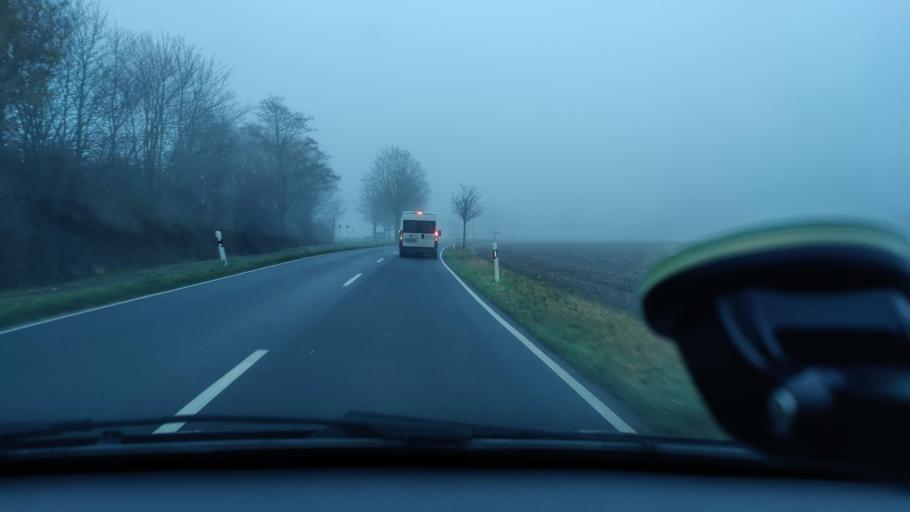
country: DE
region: North Rhine-Westphalia
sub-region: Regierungsbezirk Dusseldorf
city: Mehrhoog
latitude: 51.7024
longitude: 6.4875
